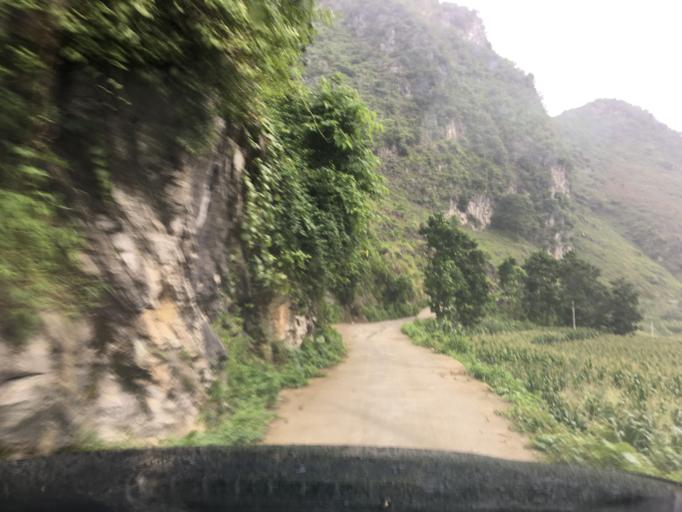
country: CN
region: Guangxi Zhuangzu Zizhiqu
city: Xinzhou
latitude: 24.9935
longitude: 105.6409
